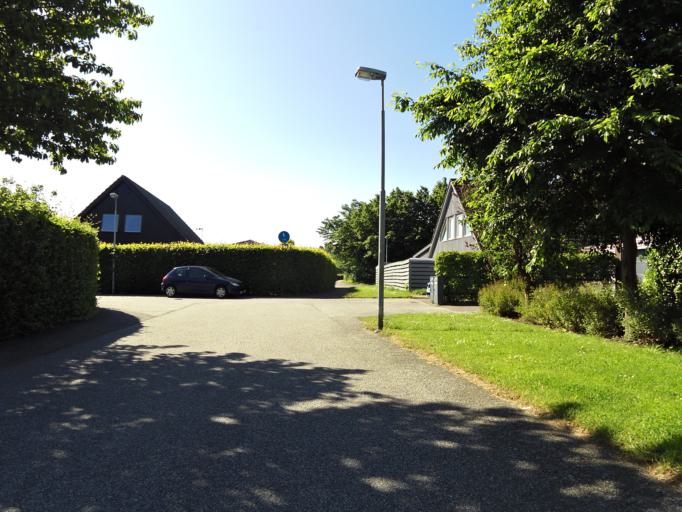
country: SE
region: Skane
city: Bjarred
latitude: 55.7207
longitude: 13.0297
